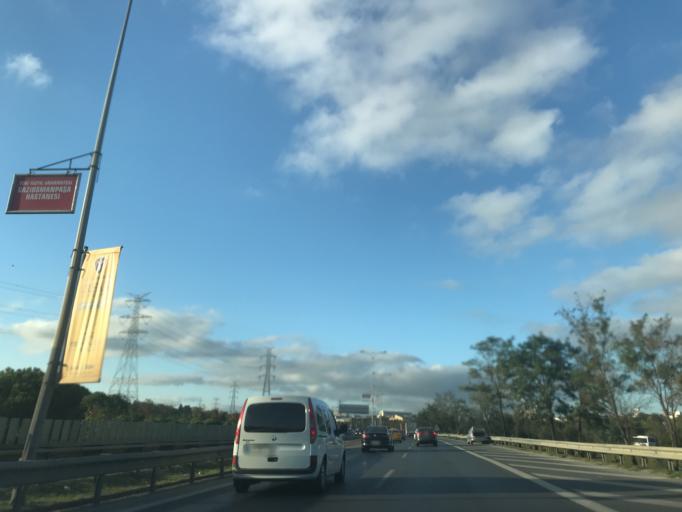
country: TR
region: Istanbul
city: Esenler
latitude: 41.0581
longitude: 28.8863
